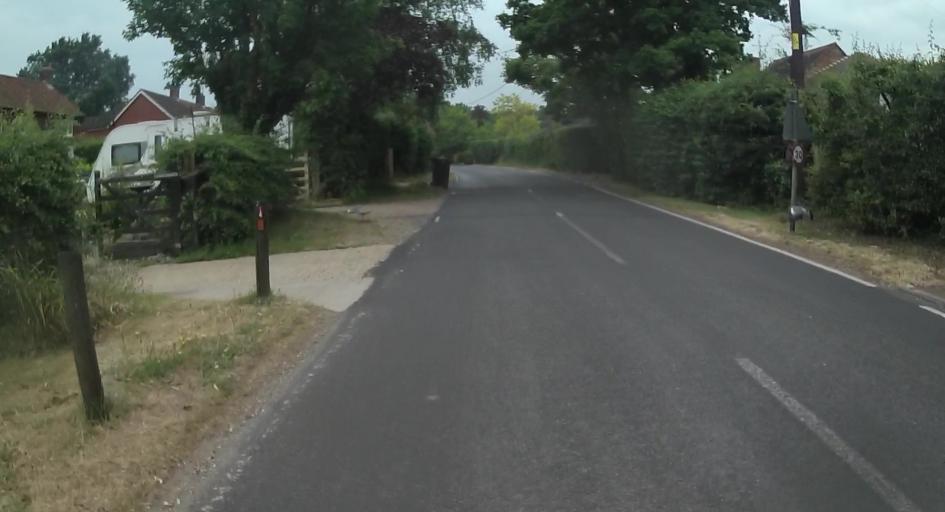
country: GB
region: England
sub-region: Hampshire
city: Fleet
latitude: 51.2802
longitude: -0.8867
